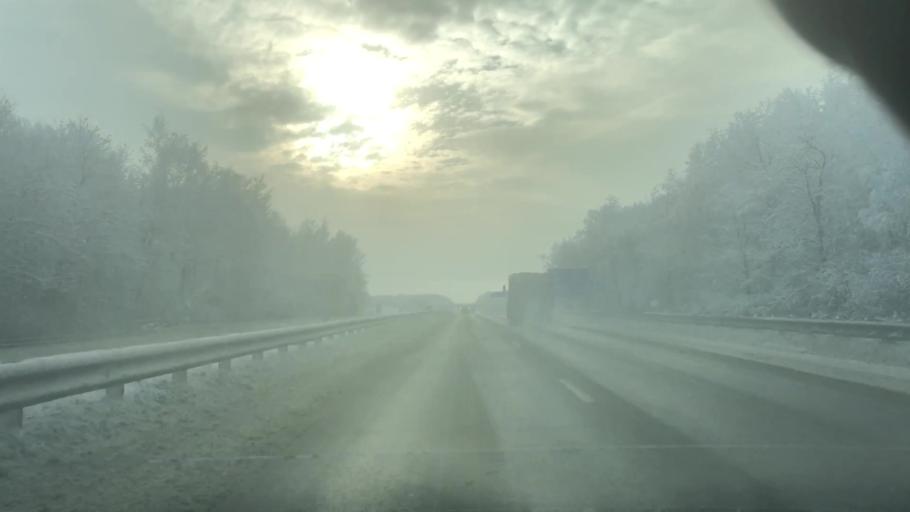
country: RU
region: Tula
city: Venev
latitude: 54.3798
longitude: 38.1550
